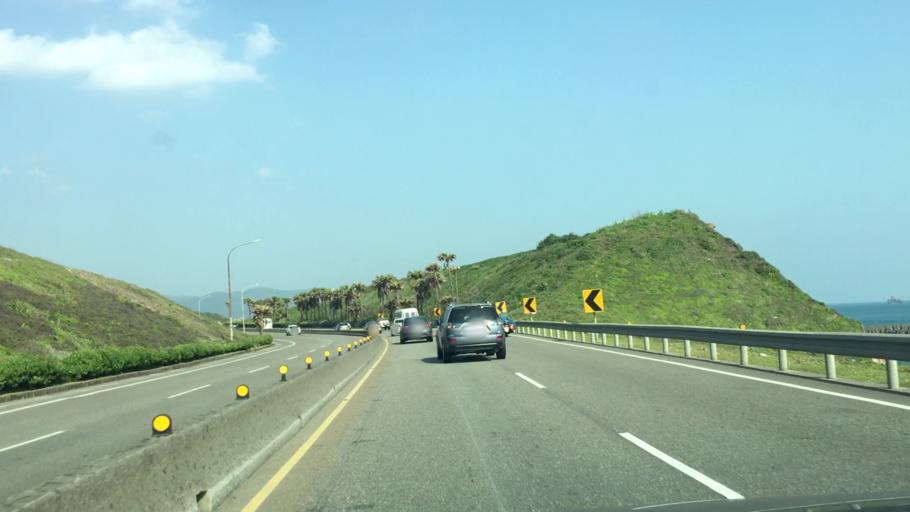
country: TW
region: Taiwan
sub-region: Keelung
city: Keelung
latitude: 25.2045
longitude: 121.6668
